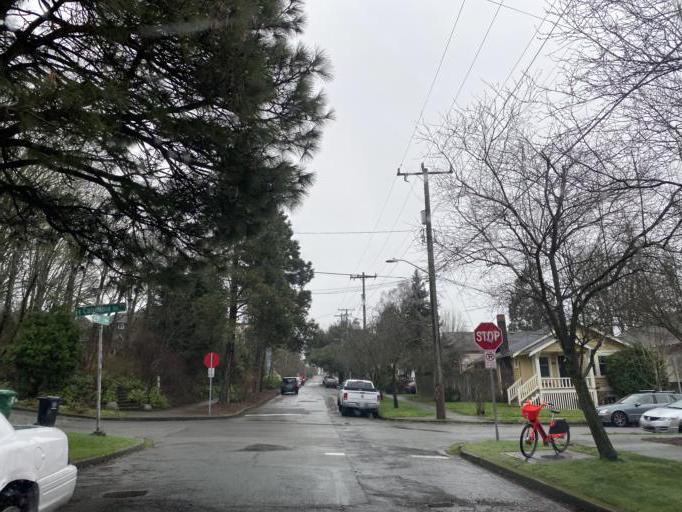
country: US
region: Washington
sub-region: King County
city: Seattle
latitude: 47.6092
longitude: -122.2950
